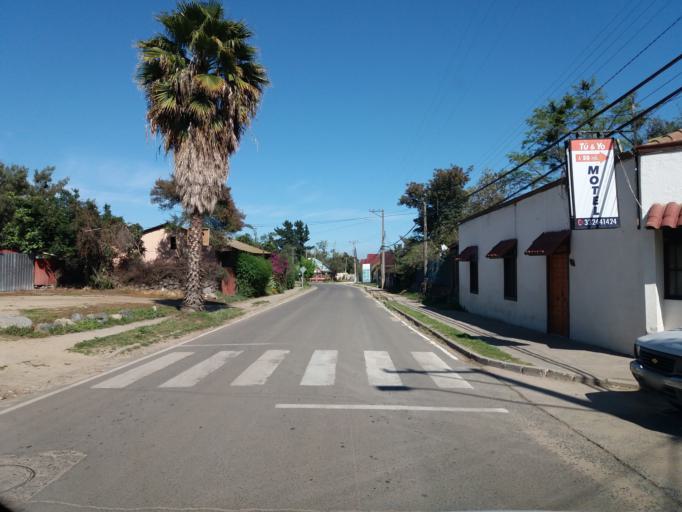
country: CL
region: Valparaiso
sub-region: Provincia de Marga Marga
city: Limache
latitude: -32.9923
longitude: -71.1661
